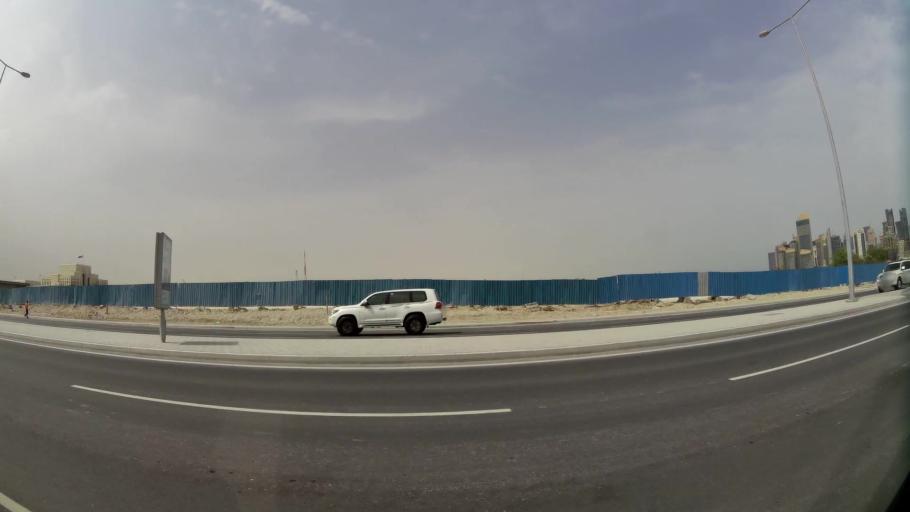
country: QA
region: Baladiyat ad Dawhah
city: Doha
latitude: 25.3029
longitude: 51.5107
